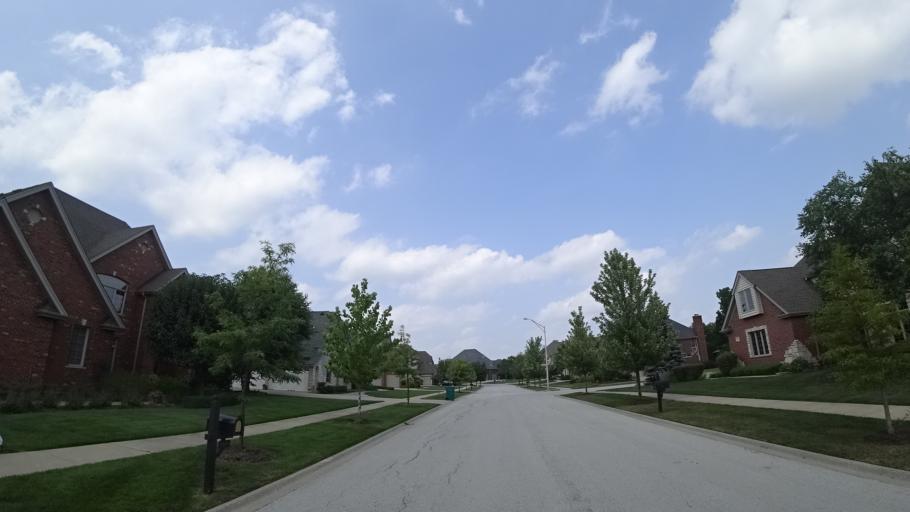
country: US
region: Illinois
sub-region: Cook County
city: Orland Park
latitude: 41.6352
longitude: -87.8883
